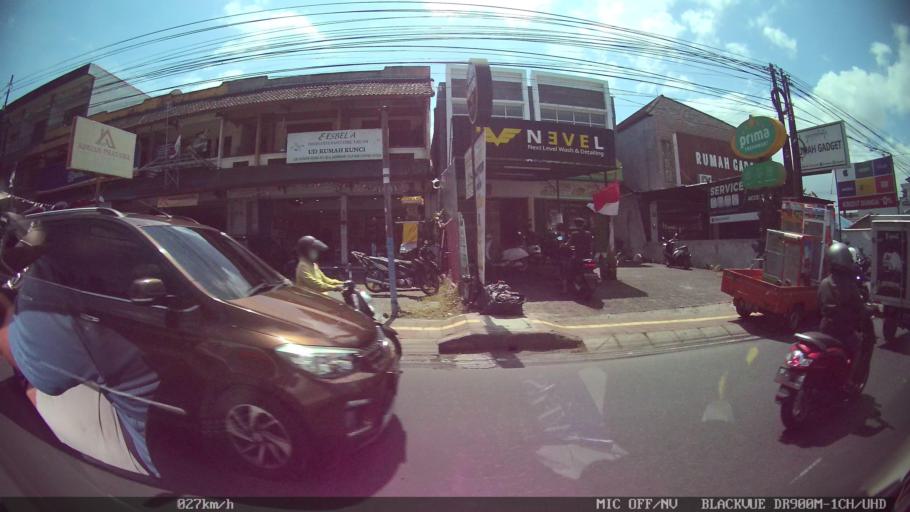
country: ID
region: Bali
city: Denpasar
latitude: -8.6517
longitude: 115.1966
